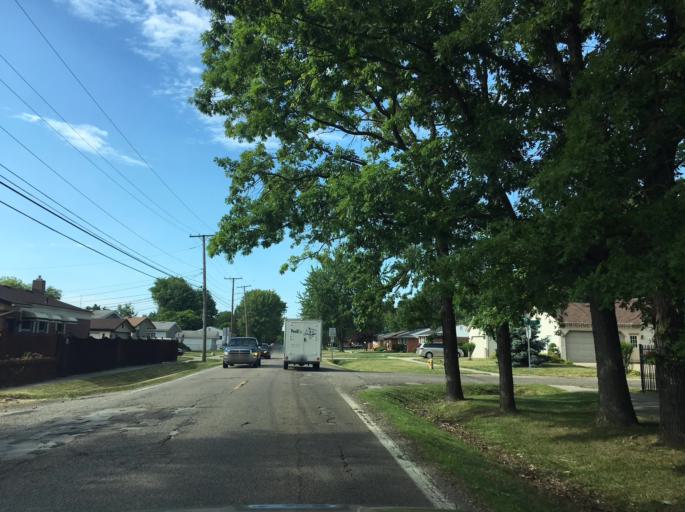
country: US
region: Michigan
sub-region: Macomb County
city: Fraser
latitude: 42.5456
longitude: -82.9199
